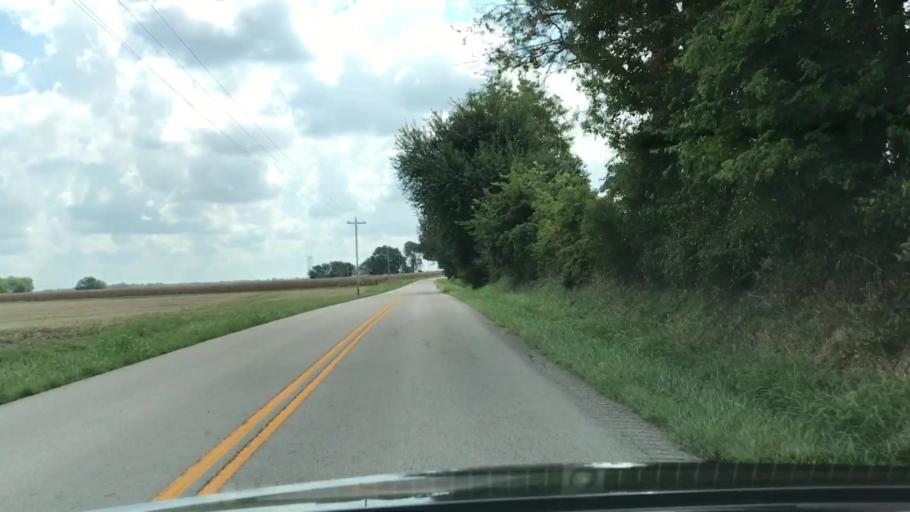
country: US
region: Kentucky
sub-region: Todd County
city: Elkton
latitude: 36.7825
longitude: -87.1249
